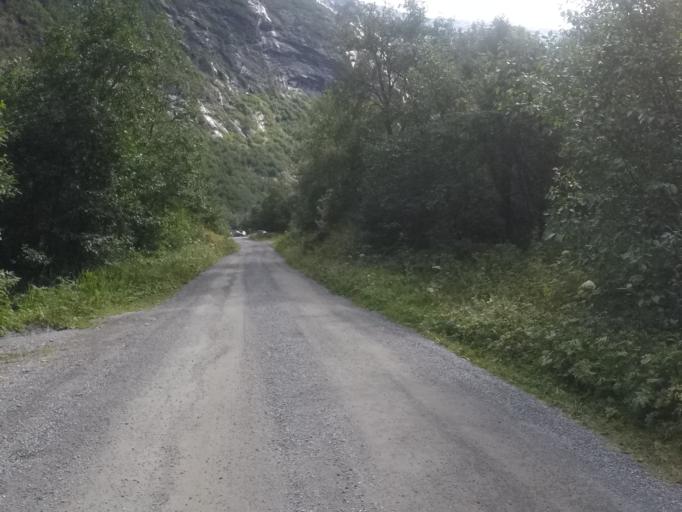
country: NO
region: Sogn og Fjordane
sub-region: Stryn
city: Stryn
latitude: 61.7481
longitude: 7.0347
